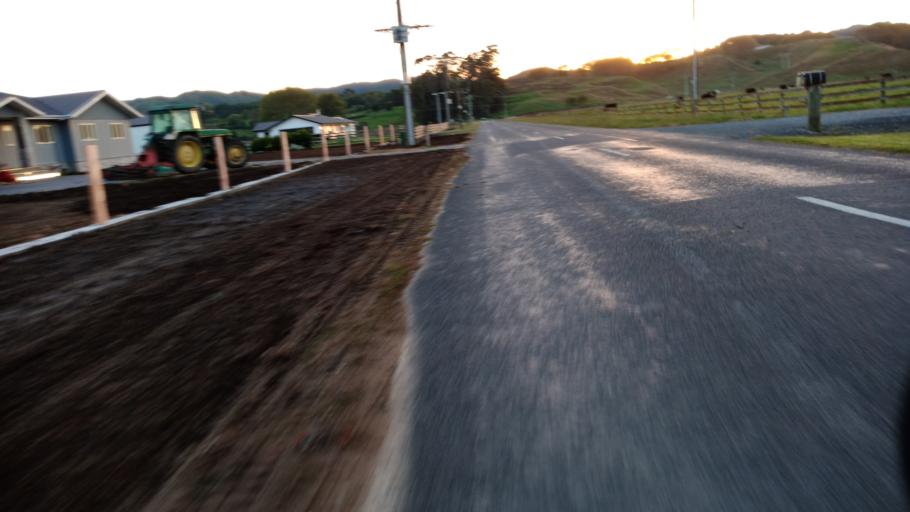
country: NZ
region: Gisborne
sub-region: Gisborne District
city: Gisborne
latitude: -38.6329
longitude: 177.9887
